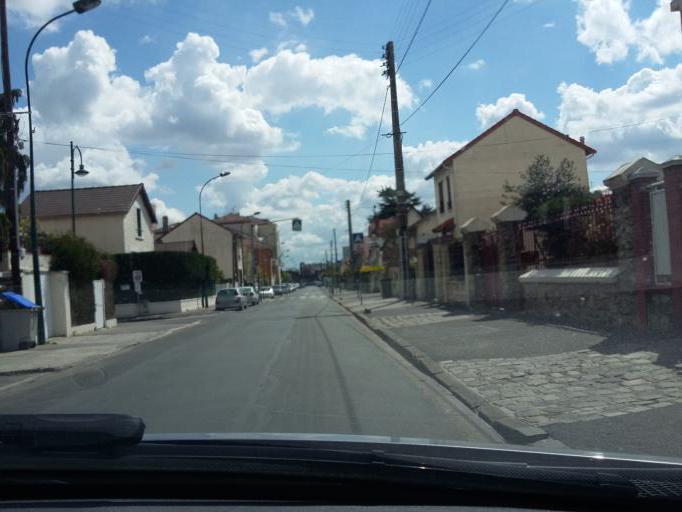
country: FR
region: Ile-de-France
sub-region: Departement de Seine-Saint-Denis
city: Epinay-sur-Seine
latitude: 48.9618
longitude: 2.3006
